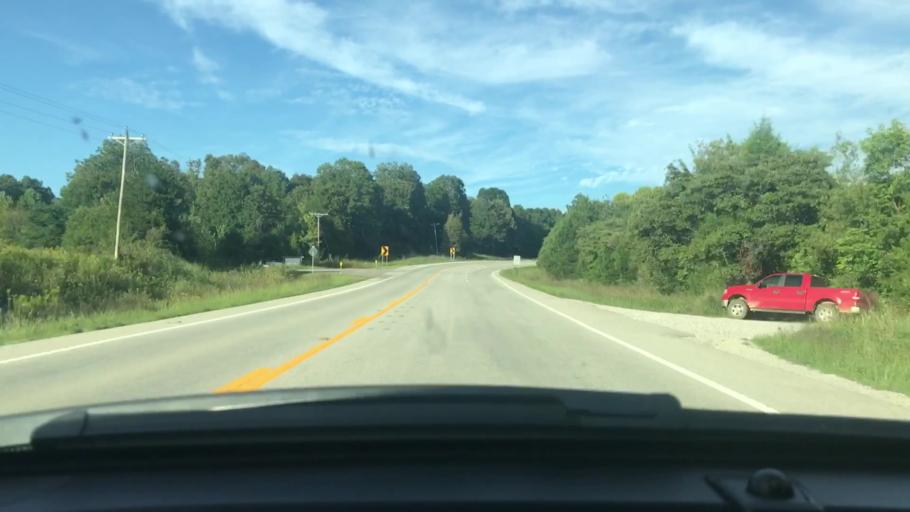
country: US
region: Arkansas
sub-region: Sharp County
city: Cherokee Village
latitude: 36.2756
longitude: -91.3293
